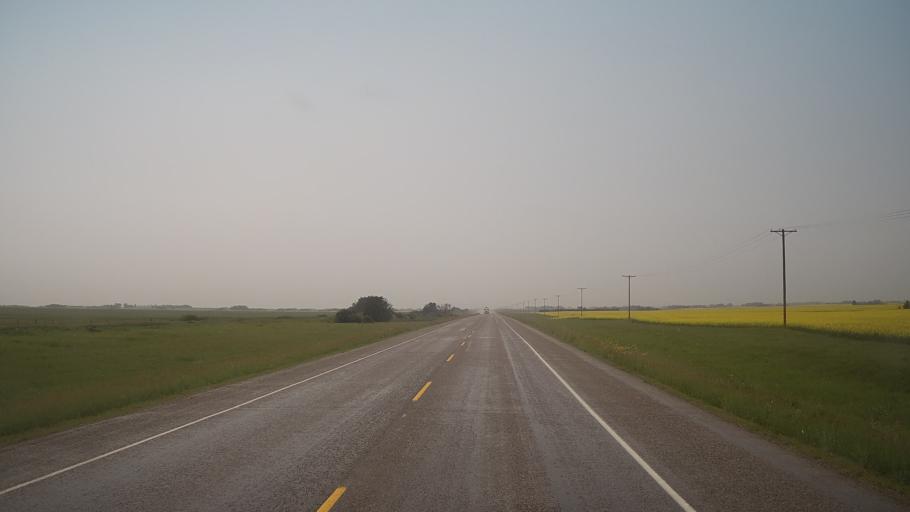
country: CA
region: Saskatchewan
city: Biggar
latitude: 52.1498
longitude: -108.2274
